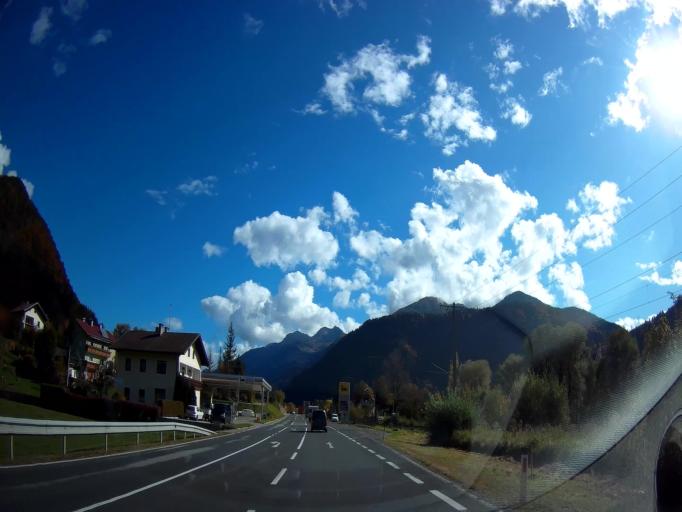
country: AT
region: Carinthia
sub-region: Politischer Bezirk Spittal an der Drau
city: Oberdrauburg
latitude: 46.7497
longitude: 12.9626
